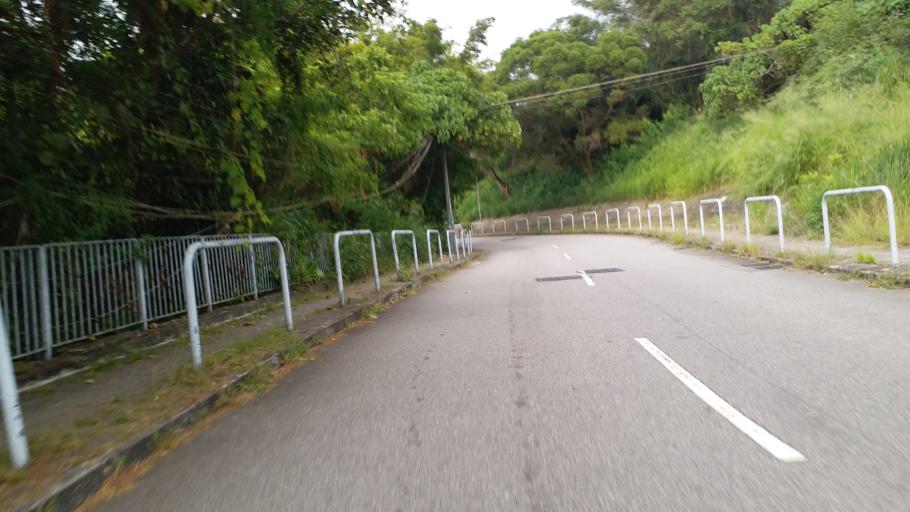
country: HK
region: Yuen Long
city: Yuen Long Kau Hui
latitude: 22.4527
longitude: 114.0104
